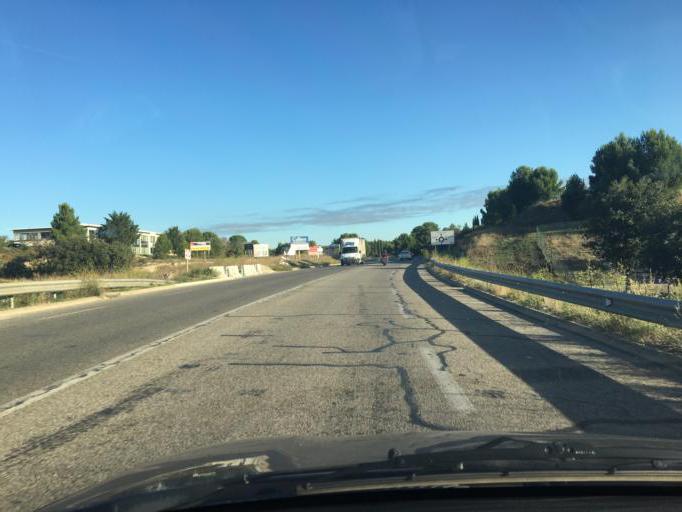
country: FR
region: Provence-Alpes-Cote d'Azur
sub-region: Departement des Bouches-du-Rhone
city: Cabries
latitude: 43.4925
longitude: 5.3506
